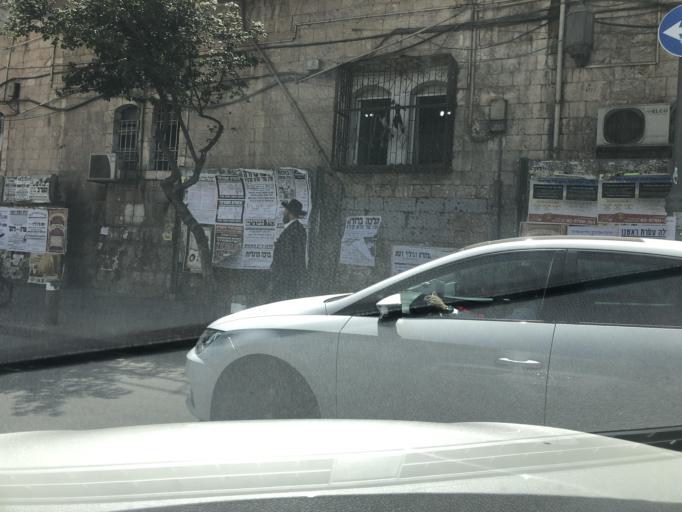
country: IL
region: Jerusalem
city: West Jerusalem
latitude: 31.7881
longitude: 35.2198
